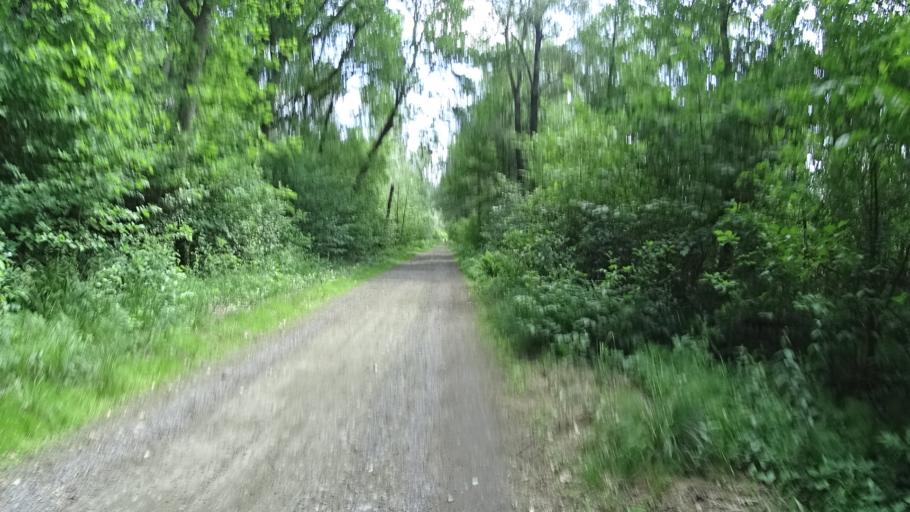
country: FI
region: Uusimaa
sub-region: Raaseporin
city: Pohja
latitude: 60.1091
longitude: 23.5488
